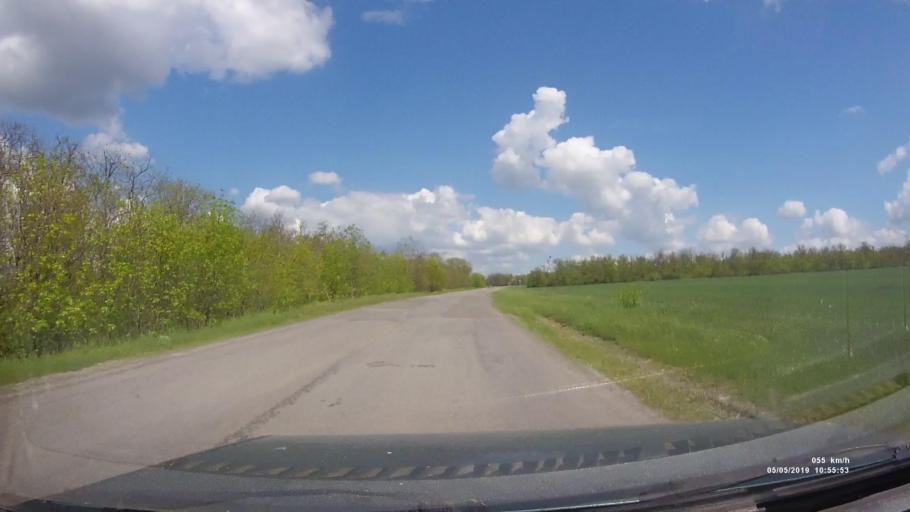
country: RU
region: Rostov
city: Ust'-Donetskiy
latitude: 47.6694
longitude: 40.8201
